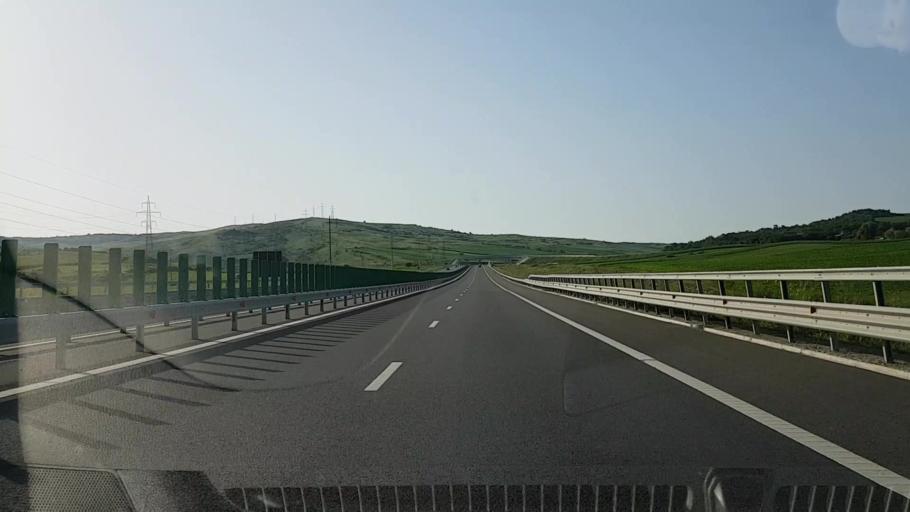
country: RO
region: Alba
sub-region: Comuna Unirea
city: Unirea
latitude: 46.4616
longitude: 23.7836
